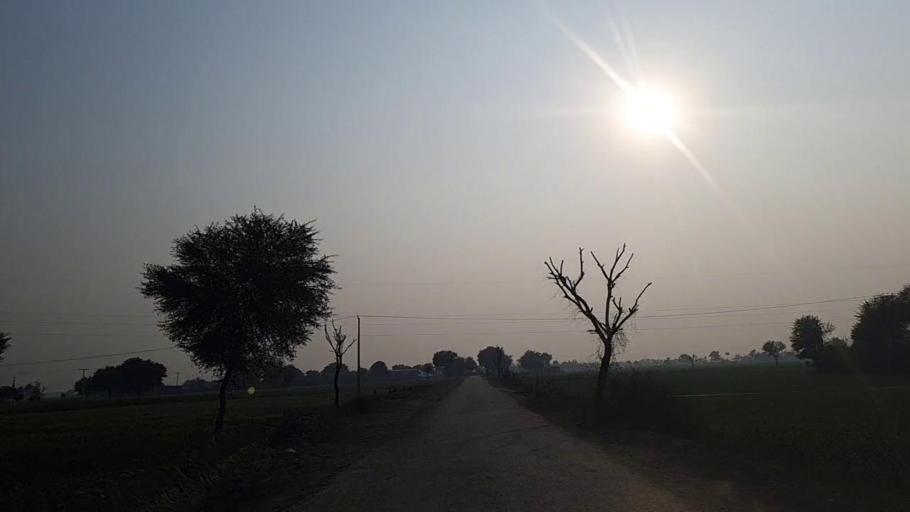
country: PK
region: Sindh
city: Nawabshah
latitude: 26.2271
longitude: 68.4817
